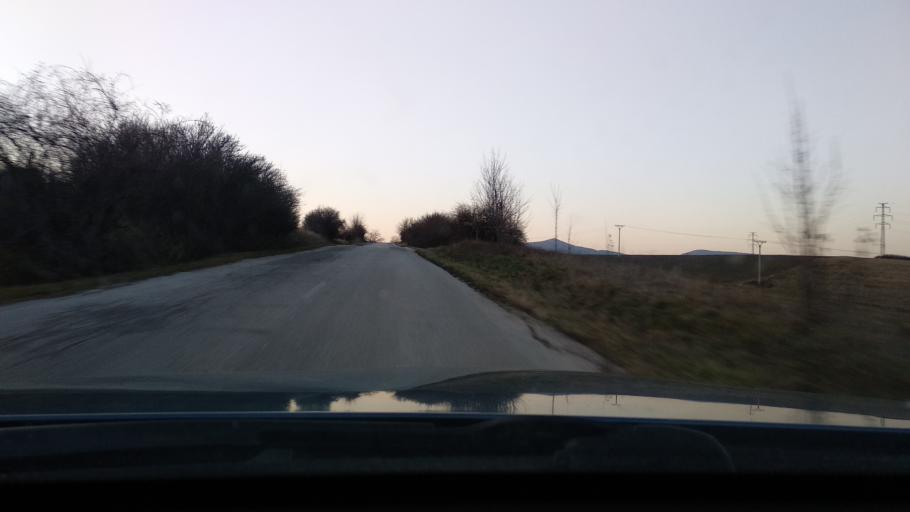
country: SK
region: Nitriansky
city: Banovce nad Bebravou
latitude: 48.7792
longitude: 18.1866
